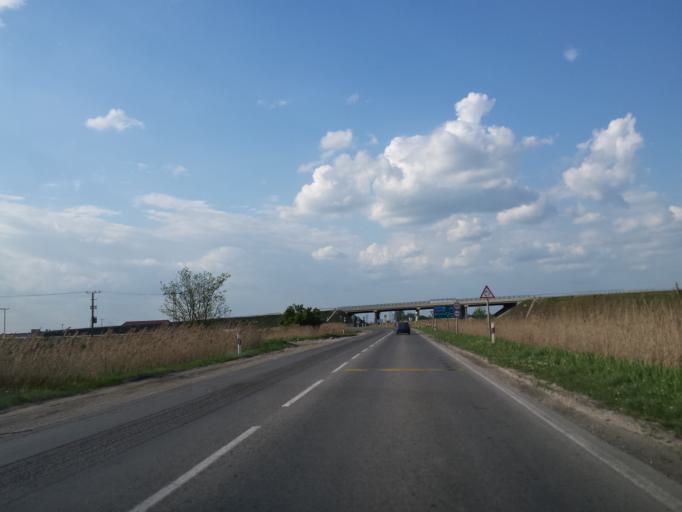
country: HU
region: Csongrad
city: Mako
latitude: 46.2649
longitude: 20.4823
